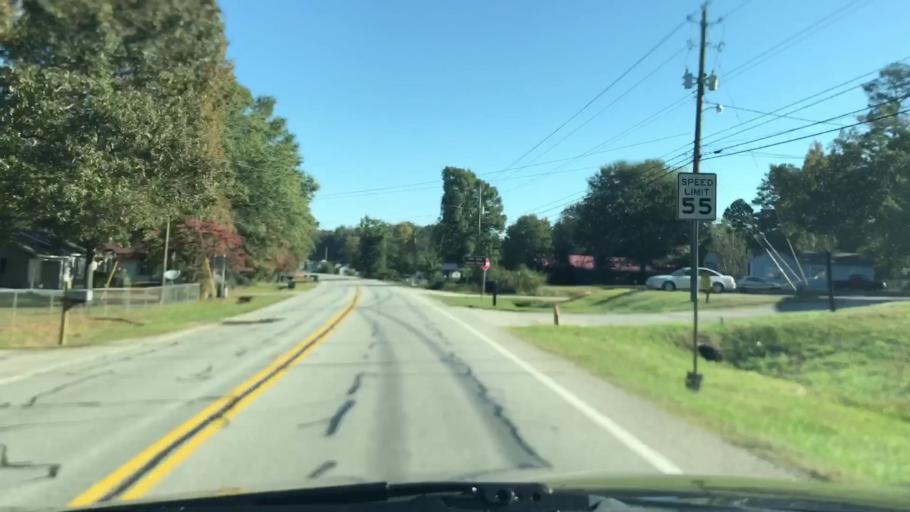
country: US
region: Georgia
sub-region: Carroll County
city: Villa Rica
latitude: 33.7509
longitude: -84.9058
